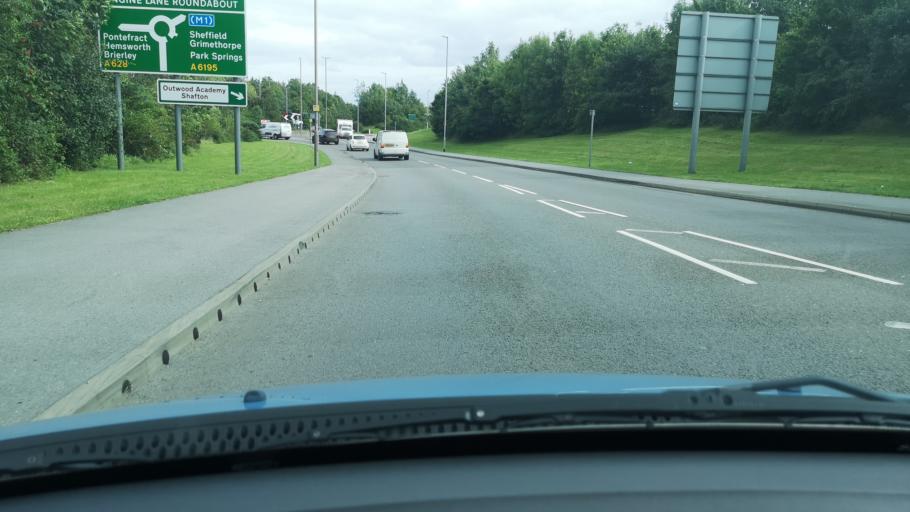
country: GB
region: England
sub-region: Barnsley
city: Shafton
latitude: 53.5878
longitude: -1.4046
